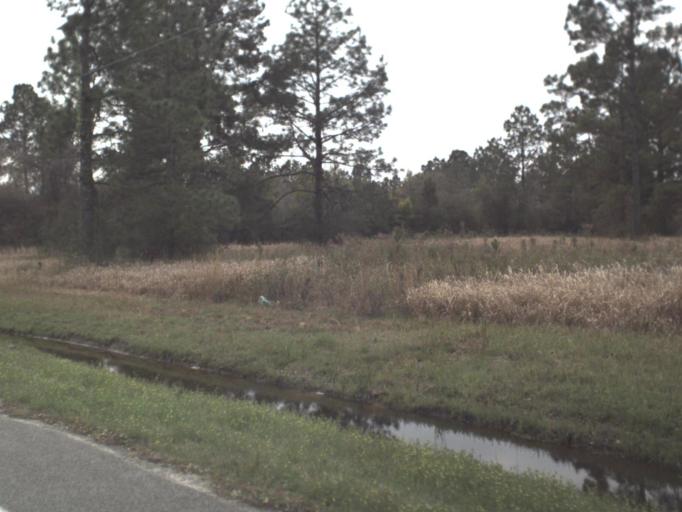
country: US
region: Florida
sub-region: Gulf County
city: Wewahitchka
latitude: 30.0346
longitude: -85.1827
